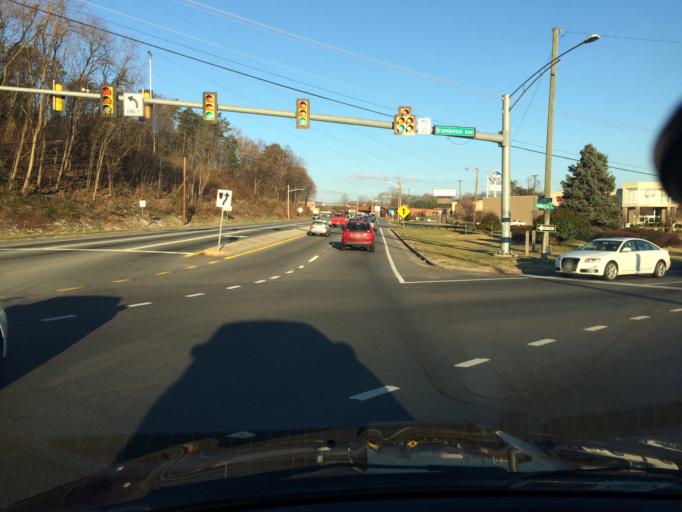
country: US
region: Virginia
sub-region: Roanoke County
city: Cave Spring
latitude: 37.2300
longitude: -80.0084
